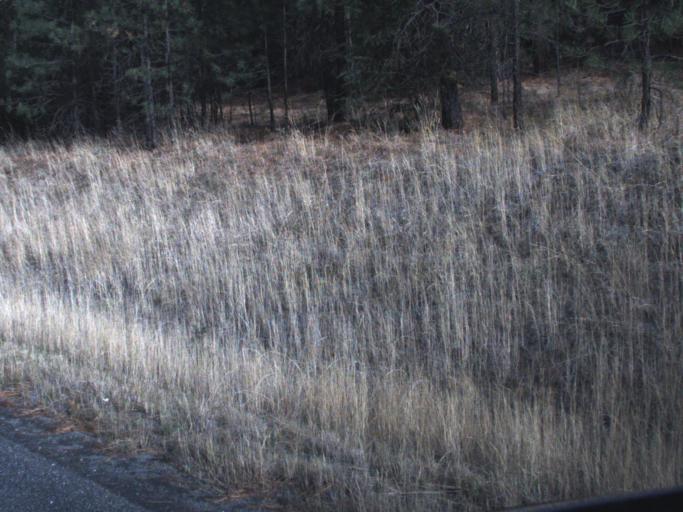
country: US
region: Washington
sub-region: Stevens County
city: Kettle Falls
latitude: 48.5221
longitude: -118.1393
